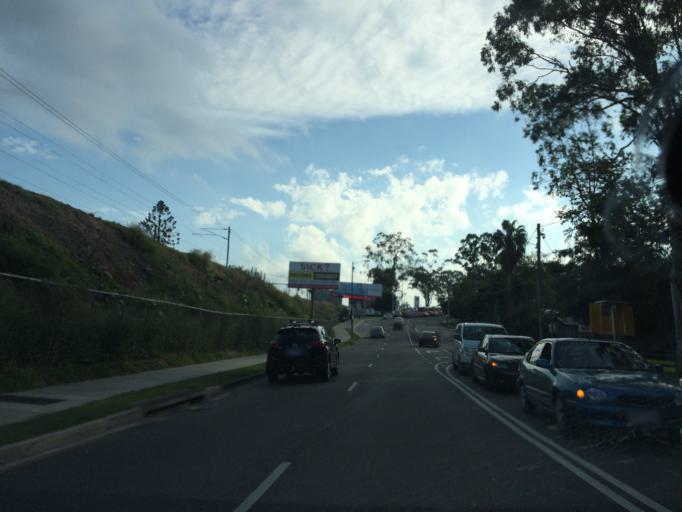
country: AU
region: Queensland
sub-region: Brisbane
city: Toowong
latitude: -27.4900
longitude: 152.9869
